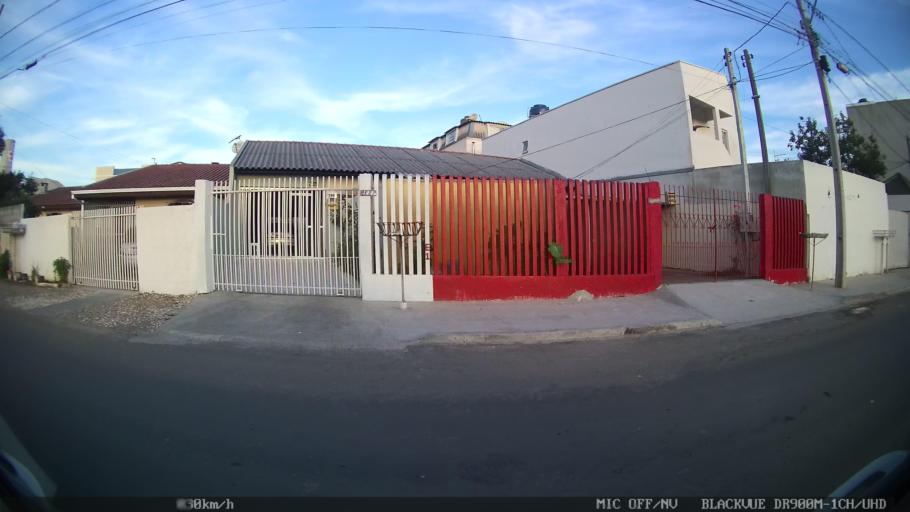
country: BR
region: Parana
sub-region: Pinhais
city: Pinhais
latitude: -25.4421
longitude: -49.1827
